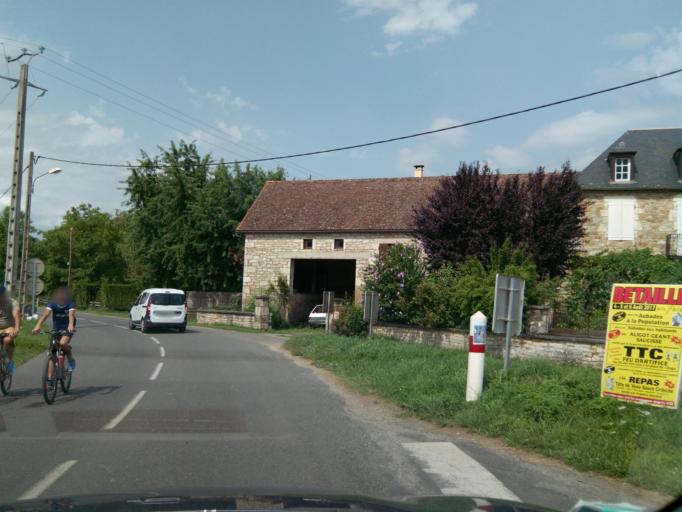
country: FR
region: Midi-Pyrenees
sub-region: Departement du Lot
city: Vayrac
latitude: 44.9159
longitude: 1.7456
